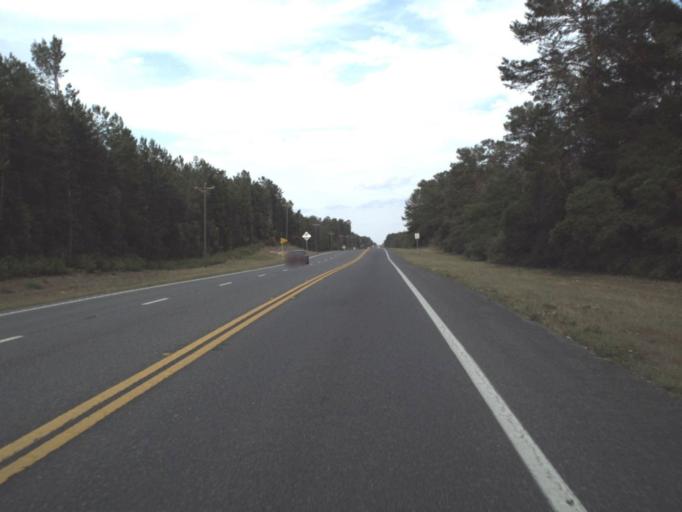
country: US
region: Florida
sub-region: Marion County
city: Silver Springs Shores
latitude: 29.1769
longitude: -81.7923
